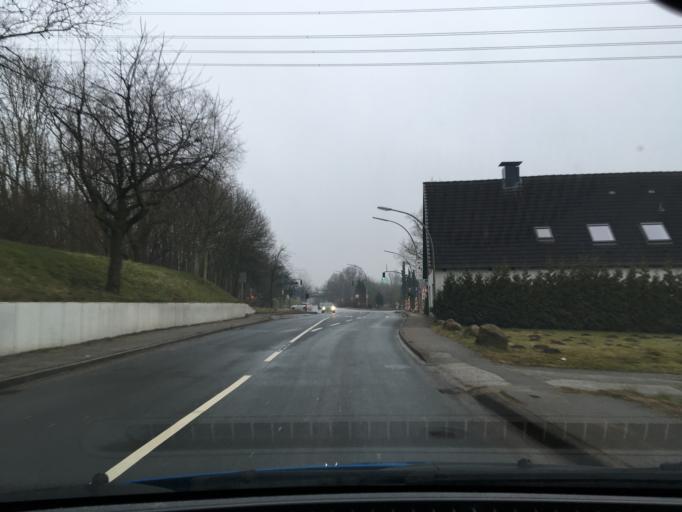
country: DE
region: Hamburg
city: Altona
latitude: 53.4959
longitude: 9.9084
